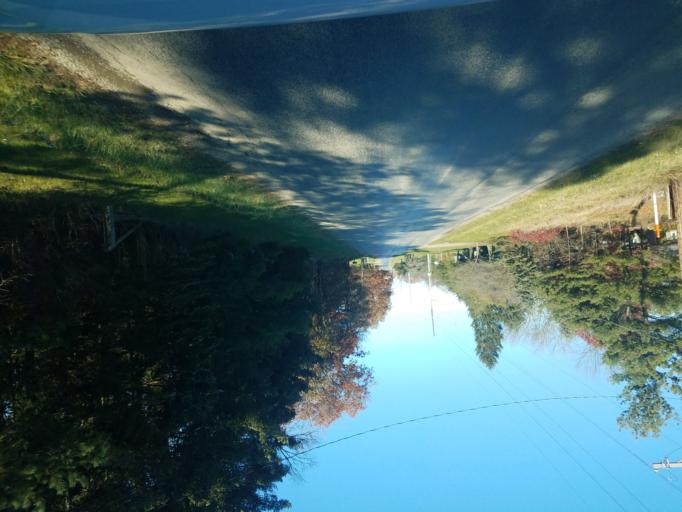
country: US
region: Ohio
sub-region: Ashland County
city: Ashland
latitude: 40.8248
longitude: -82.3493
